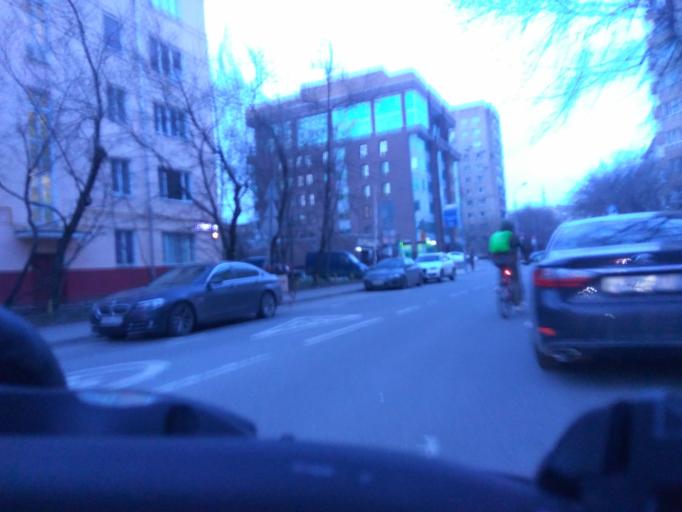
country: RU
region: Moskovskaya
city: Presnenskiy
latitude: 55.7425
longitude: 37.5491
